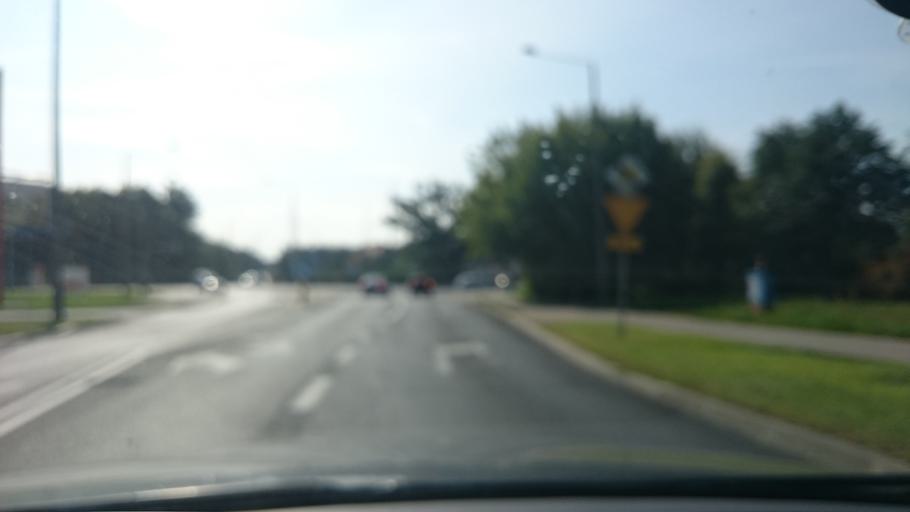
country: PL
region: Kujawsko-Pomorskie
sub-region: Grudziadz
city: Grudziadz
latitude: 53.4529
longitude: 18.7316
